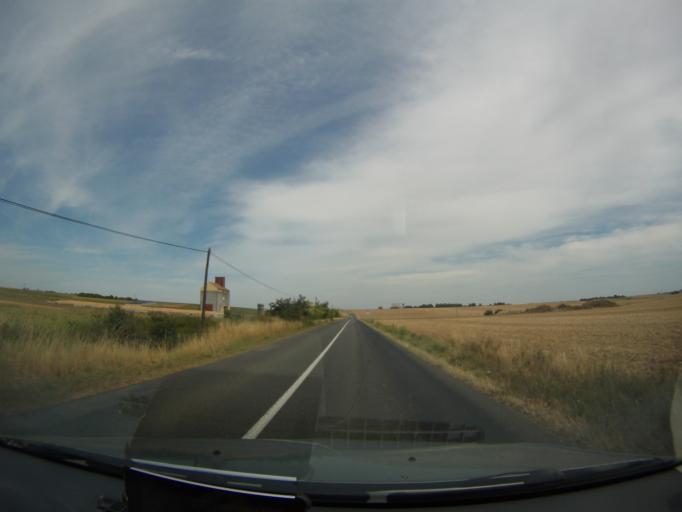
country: FR
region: Poitou-Charentes
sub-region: Departement de la Vienne
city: Saint-Jean-de-Sauves
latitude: 46.8012
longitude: 0.0857
